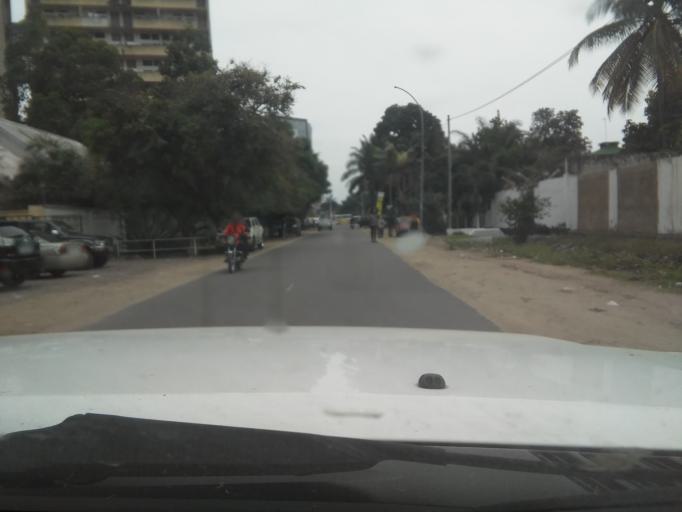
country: CD
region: Kinshasa
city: Kinshasa
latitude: -4.3134
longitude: 15.2870
